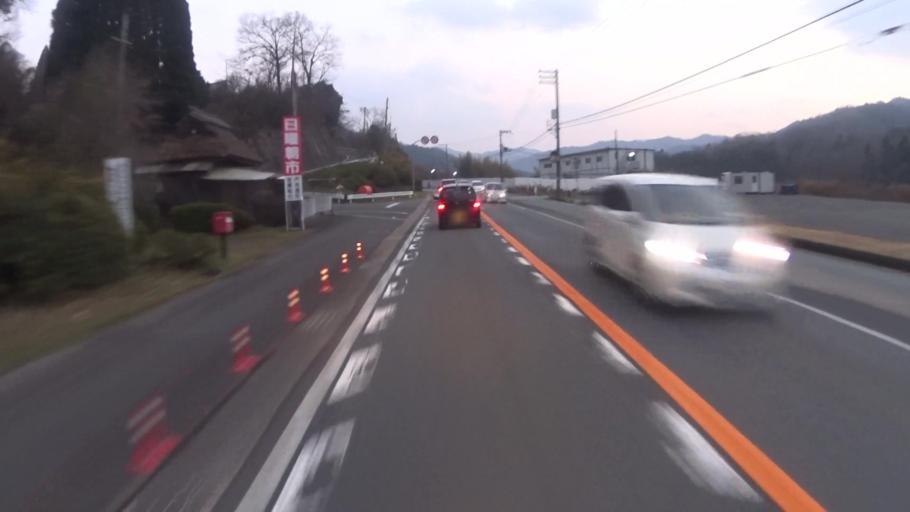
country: JP
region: Kyoto
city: Ayabe
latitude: 35.2918
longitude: 135.3314
